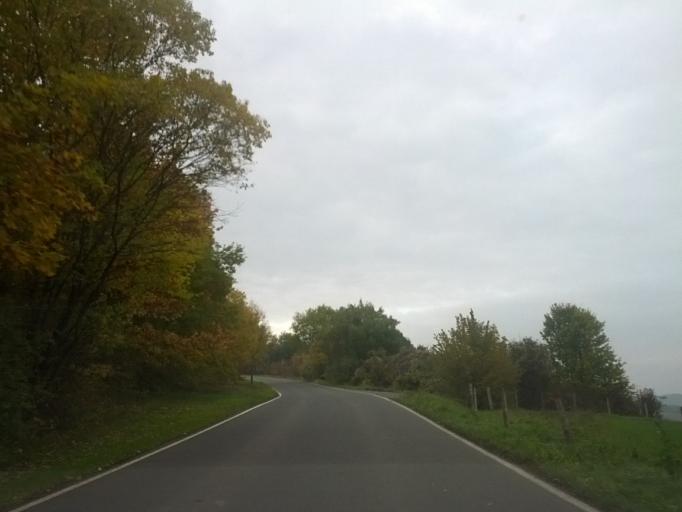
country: DE
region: Thuringia
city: Creuzburg
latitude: 51.0244
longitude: 10.2171
